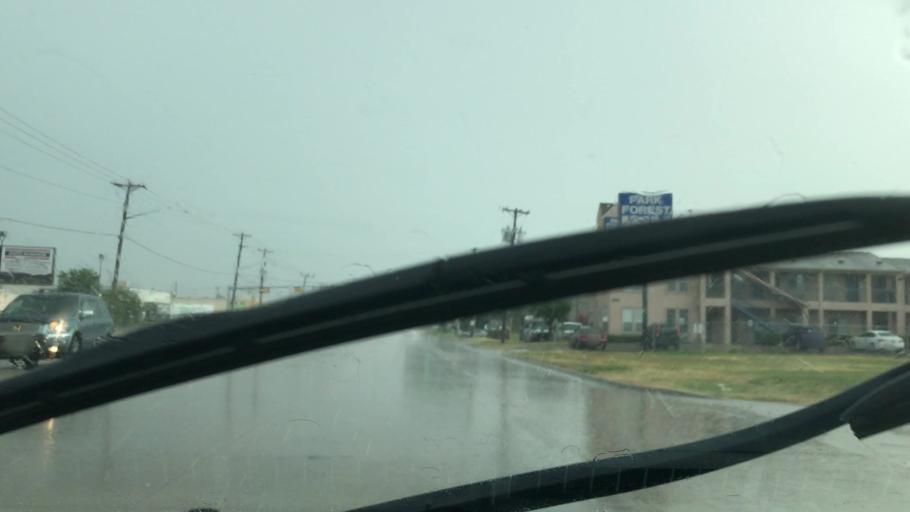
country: US
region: Texas
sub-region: Dallas County
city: Richardson
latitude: 32.9053
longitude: -96.7006
